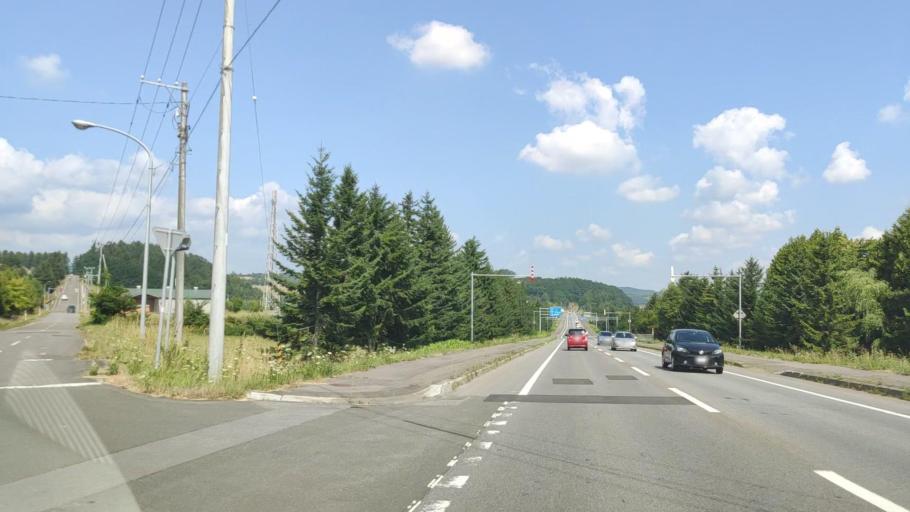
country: JP
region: Hokkaido
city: Shimo-furano
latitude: 43.4635
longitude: 142.4568
